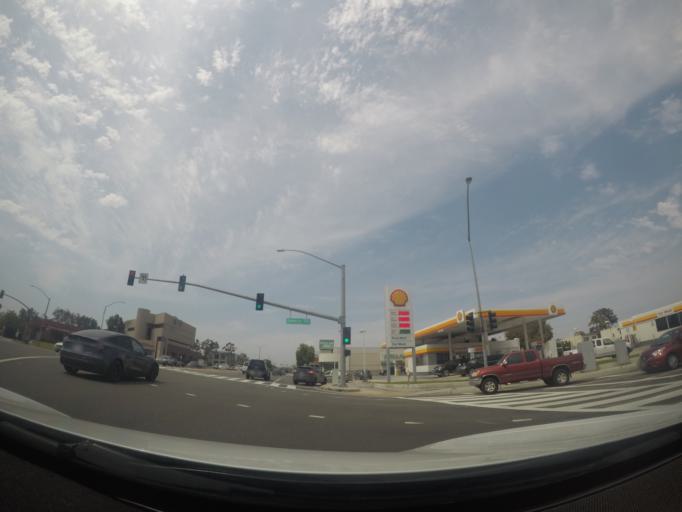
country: US
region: California
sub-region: Los Angeles County
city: Torrance
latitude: 33.8158
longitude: -118.3510
